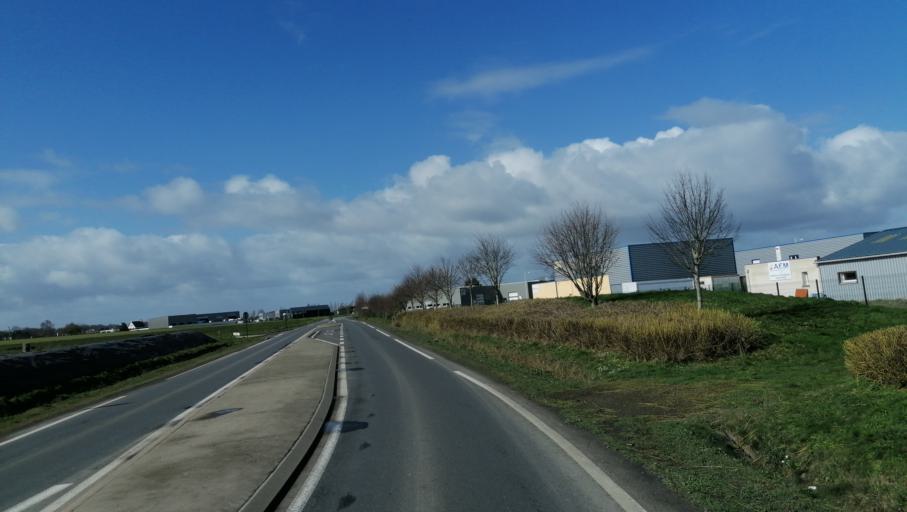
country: FR
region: Brittany
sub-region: Departement des Cotes-d'Armor
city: Tremuson
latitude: 48.5288
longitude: -2.8513
